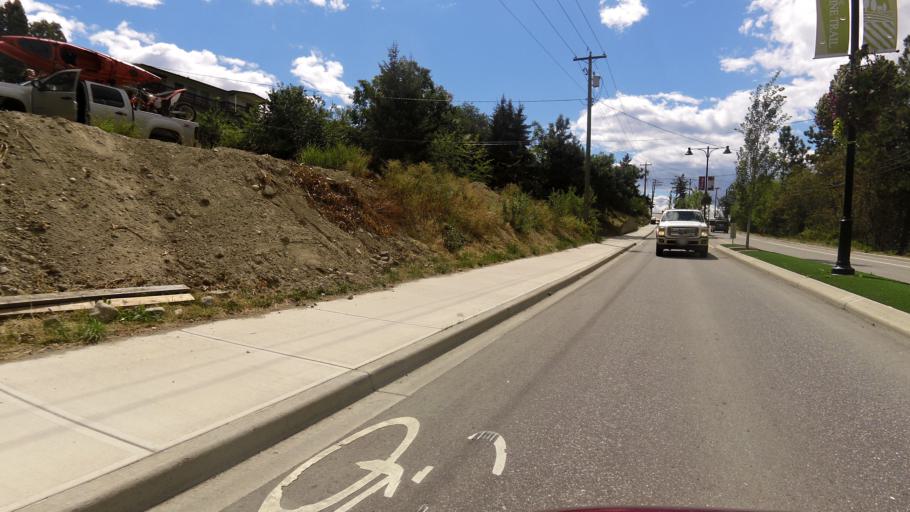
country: CA
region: British Columbia
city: West Kelowna
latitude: 49.8673
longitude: -119.5540
